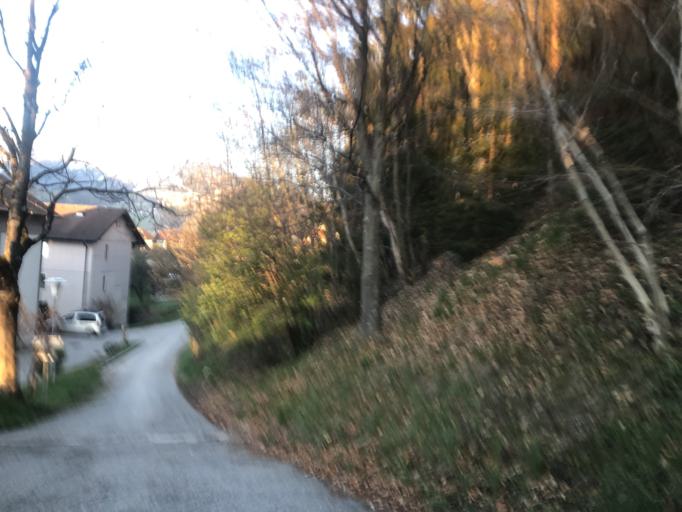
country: AT
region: Styria
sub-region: Politischer Bezirk Liezen
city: Schladming
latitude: 47.4012
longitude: 13.7006
